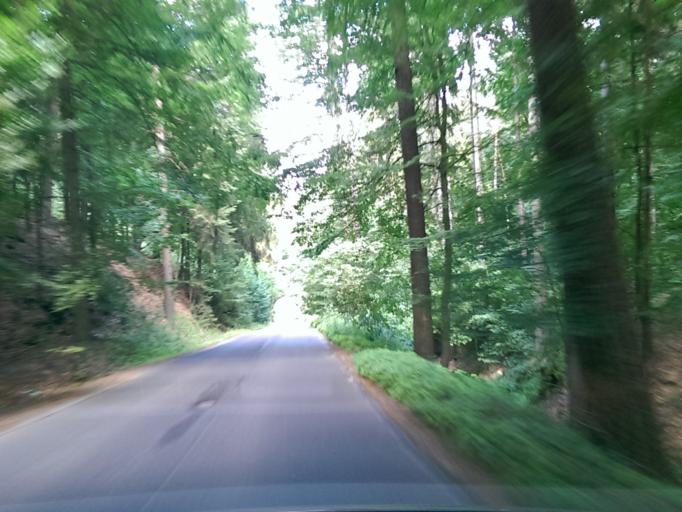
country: CZ
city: Duba
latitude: 50.5046
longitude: 14.5741
